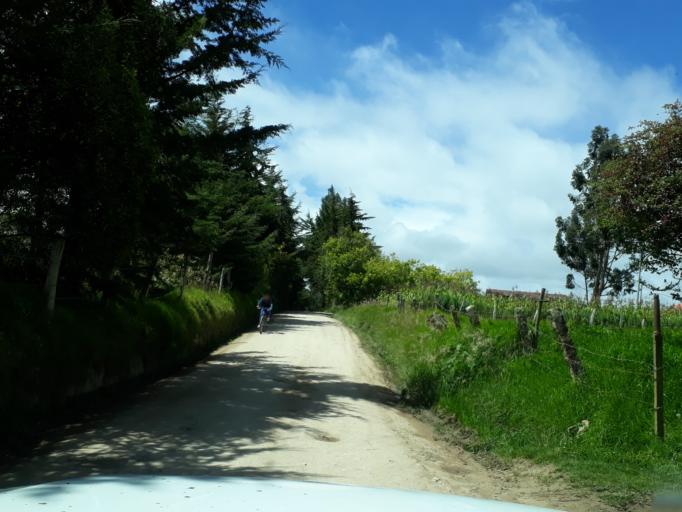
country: CO
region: Cundinamarca
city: Guasca
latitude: 4.8459
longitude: -73.8847
